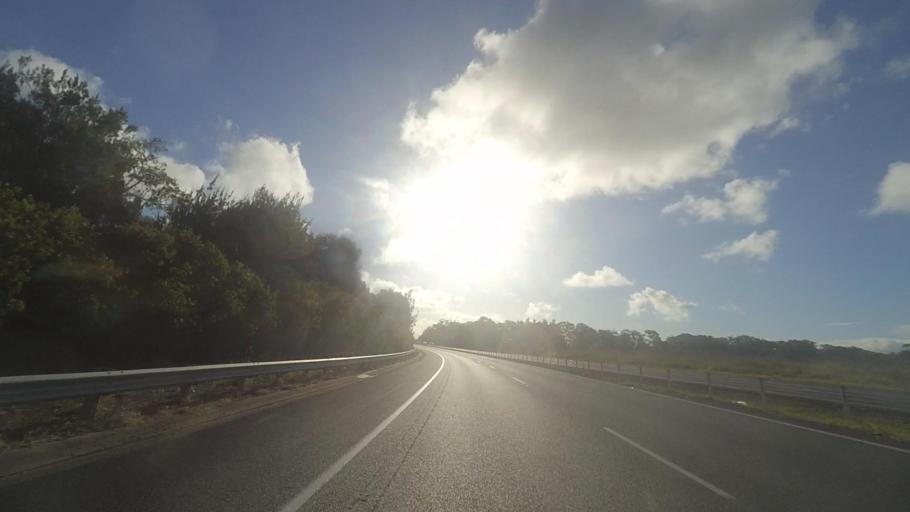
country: AU
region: New South Wales
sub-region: Great Lakes
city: Nabiac
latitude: -32.0926
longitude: 152.3873
